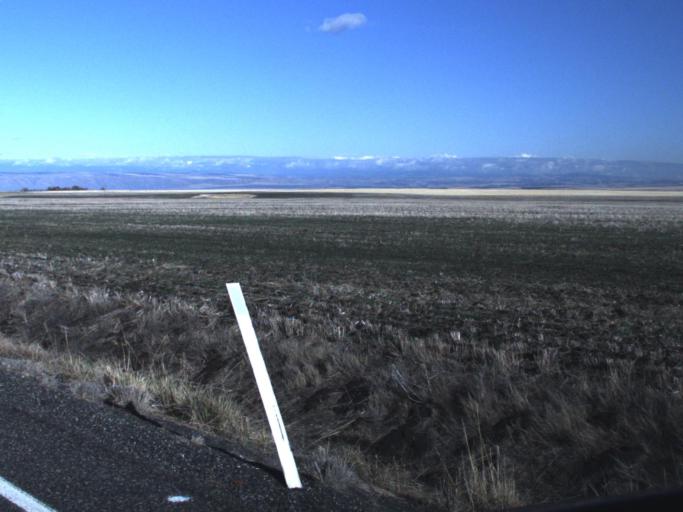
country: US
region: Washington
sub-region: Asotin County
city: Asotin
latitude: 46.2157
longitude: -117.0703
